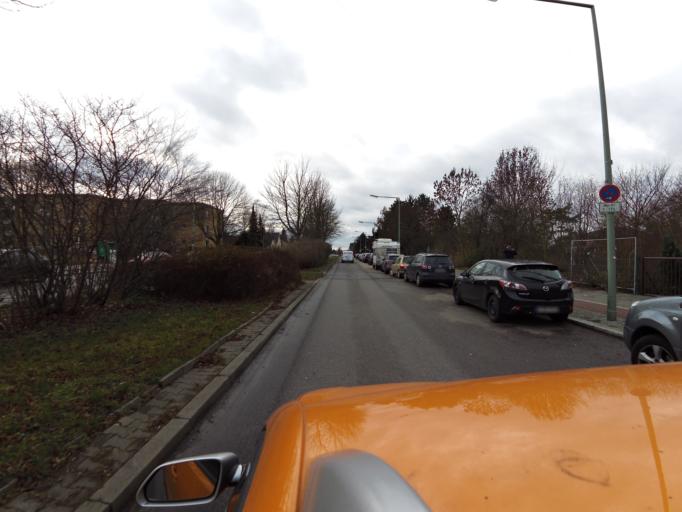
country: DE
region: Berlin
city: Rudow
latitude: 52.4187
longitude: 13.4788
